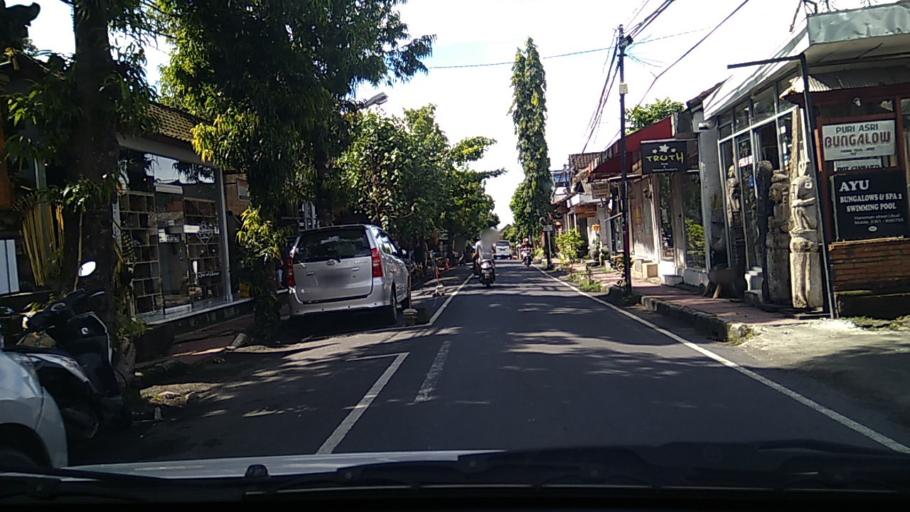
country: ID
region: Bali
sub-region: Kabupaten Gianyar
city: Ubud
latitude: -8.5123
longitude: 115.2644
